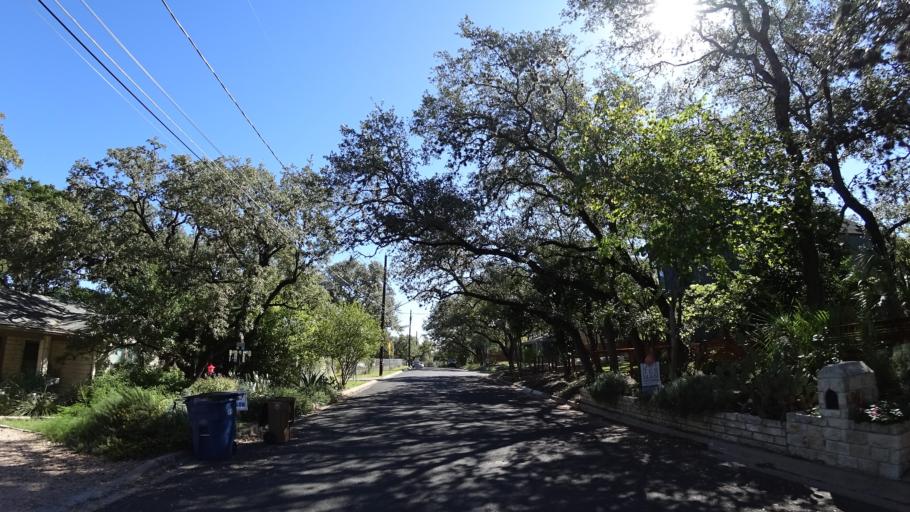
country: US
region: Texas
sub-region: Travis County
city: Austin
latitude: 30.2405
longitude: -97.7641
